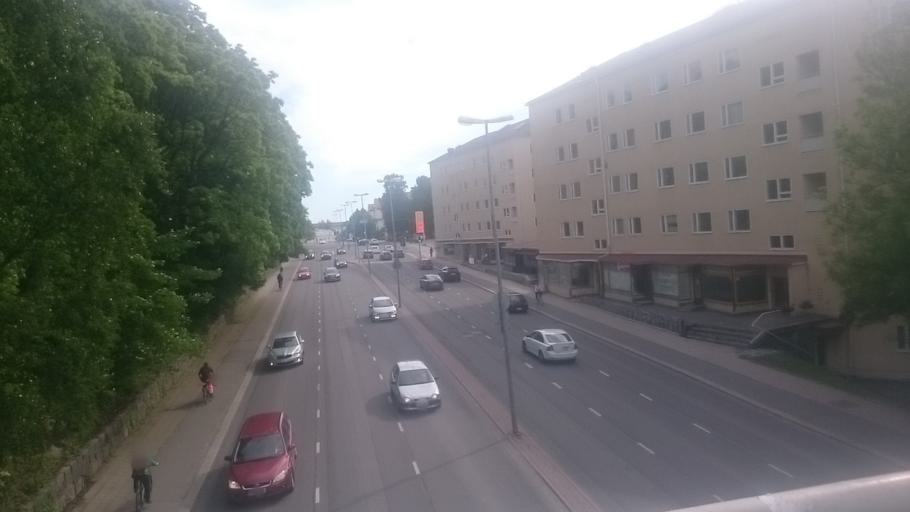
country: FI
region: Varsinais-Suomi
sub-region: Turku
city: Turku
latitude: 60.4423
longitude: 22.2582
